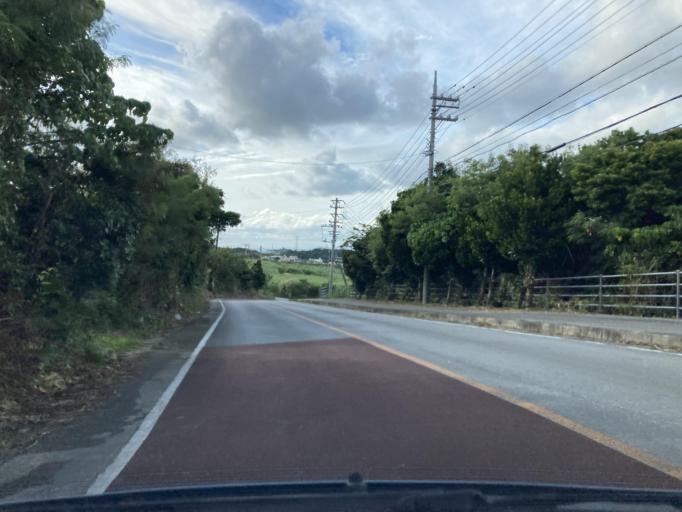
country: JP
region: Okinawa
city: Itoman
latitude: 26.1318
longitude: 127.7100
